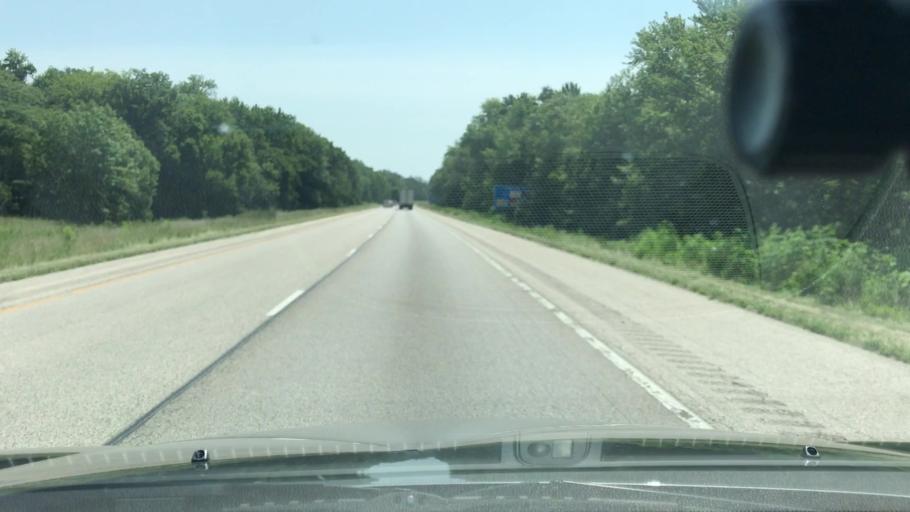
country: US
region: Illinois
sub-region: Washington County
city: Nashville
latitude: 38.4008
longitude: -89.4002
